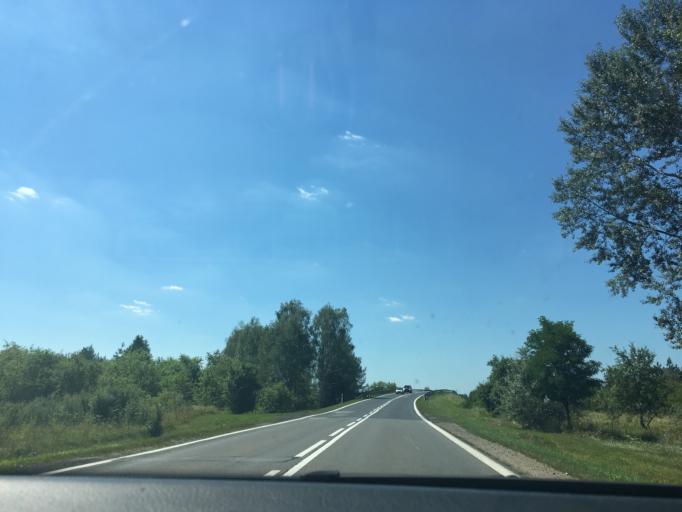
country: PL
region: Subcarpathian Voivodeship
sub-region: Powiat nizanski
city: Nisko
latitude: 50.5131
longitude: 22.1508
